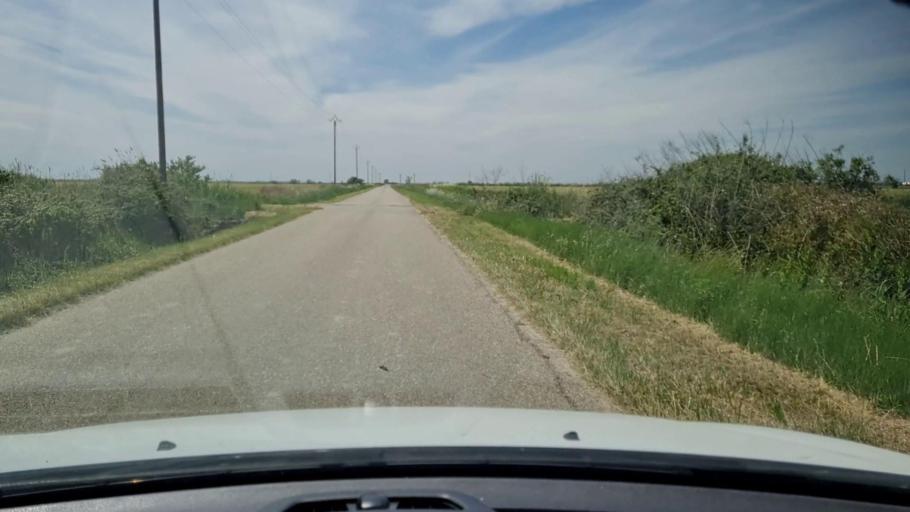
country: FR
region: Languedoc-Roussillon
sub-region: Departement du Gard
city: Saint-Gilles
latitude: 43.6029
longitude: 4.4448
